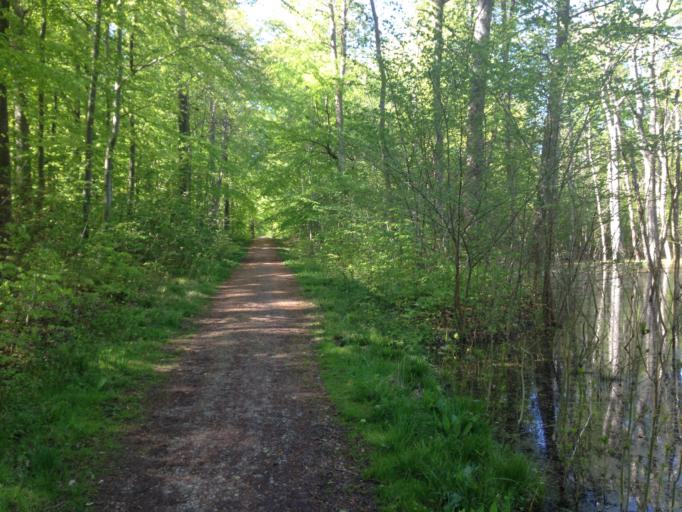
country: DK
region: Capital Region
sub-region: Fredensborg Kommune
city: Niva
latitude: 55.9434
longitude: 12.5210
